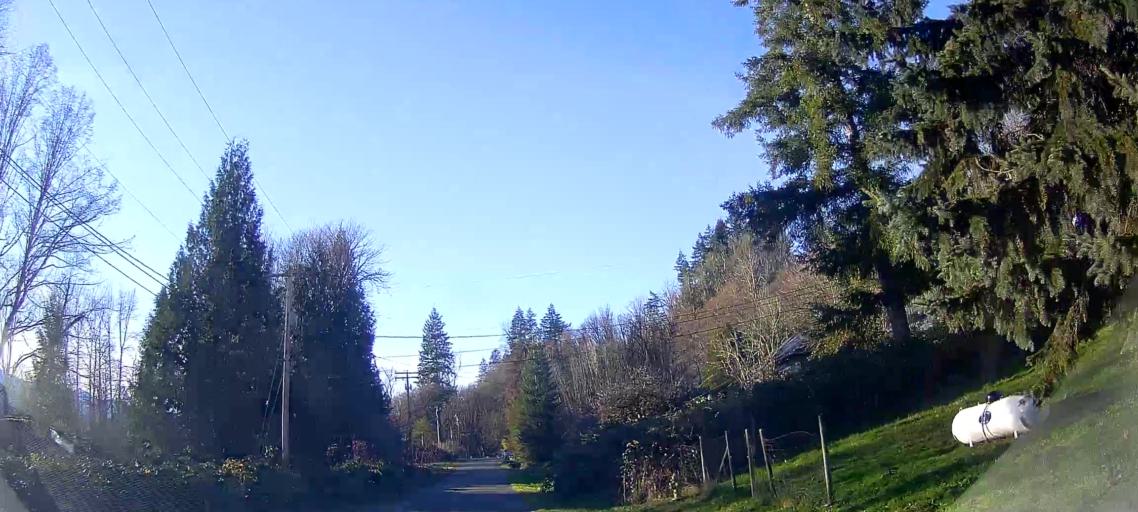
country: US
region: Washington
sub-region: Snohomish County
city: Darrington
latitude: 48.5399
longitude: -121.7564
